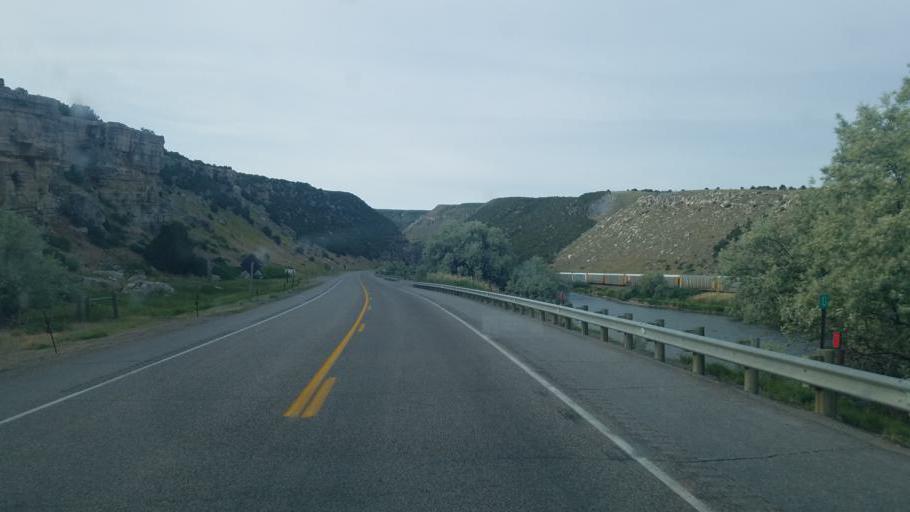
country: US
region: Wyoming
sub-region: Hot Springs County
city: Thermopolis
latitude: 43.5829
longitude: -108.2136
